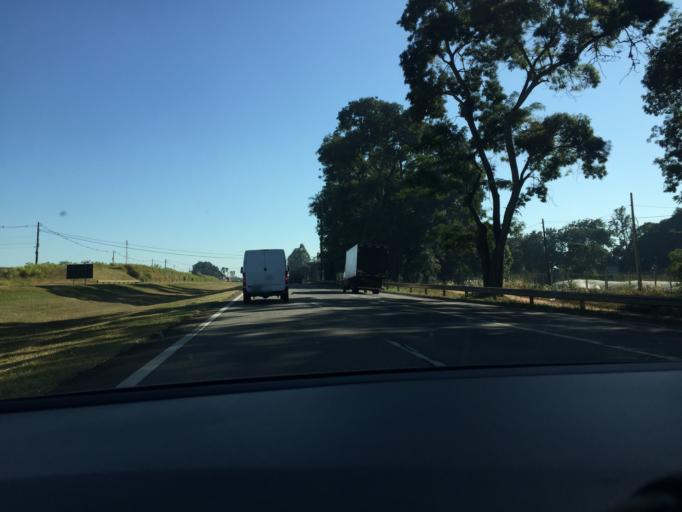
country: BR
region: Sao Paulo
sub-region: Santo Antonio De Posse
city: Santo Antonio de Posse
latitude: -22.6190
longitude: -47.0068
